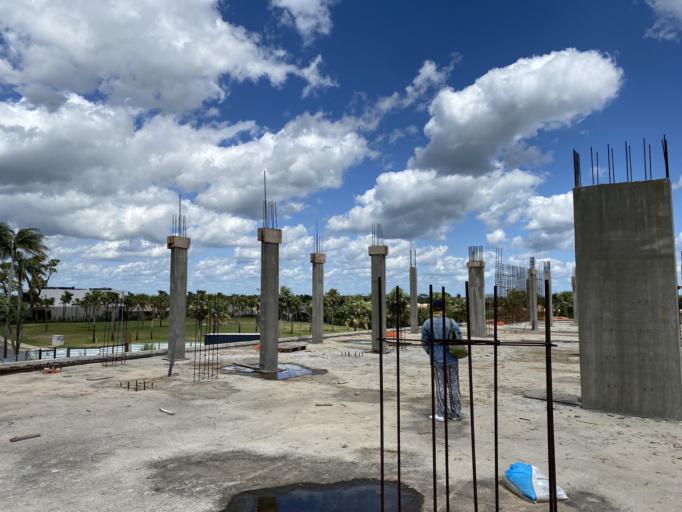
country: PY
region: Central
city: Colonia Mariano Roque Alonso
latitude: -25.1875
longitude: -57.5560
